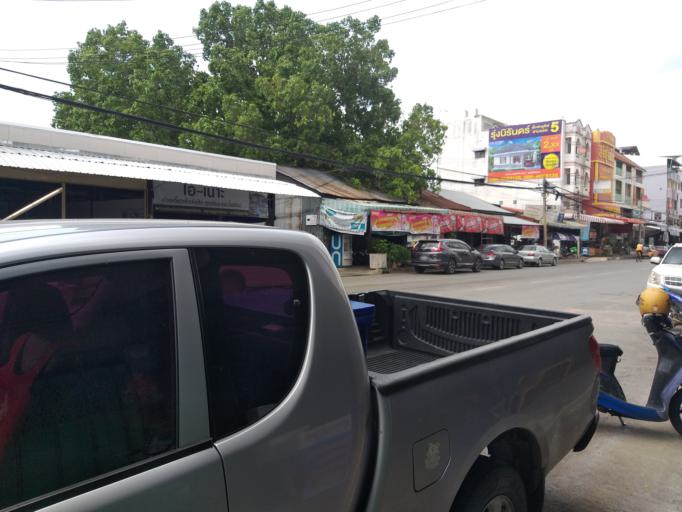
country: TH
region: Nakhon Ratchasima
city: Nakhon Ratchasima
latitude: 14.9746
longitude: 102.0893
